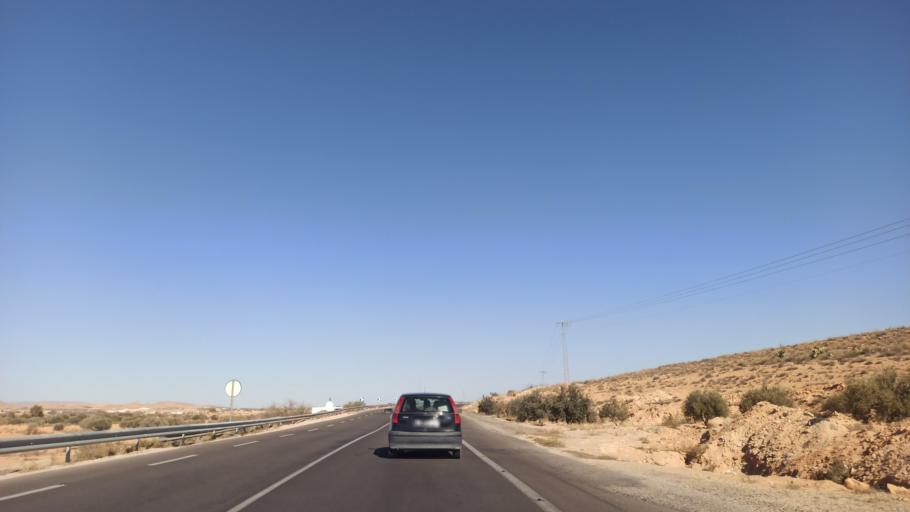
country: TN
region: Sidi Bu Zayd
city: Bi'r al Hufayy
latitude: 34.7226
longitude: 9.0613
